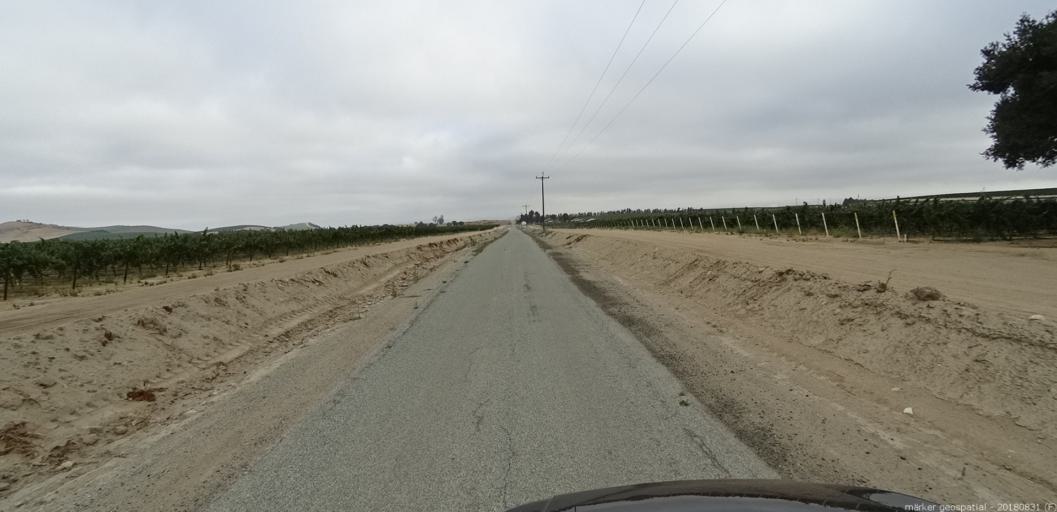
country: US
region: California
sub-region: Monterey County
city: King City
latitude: 36.1158
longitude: -121.0874
